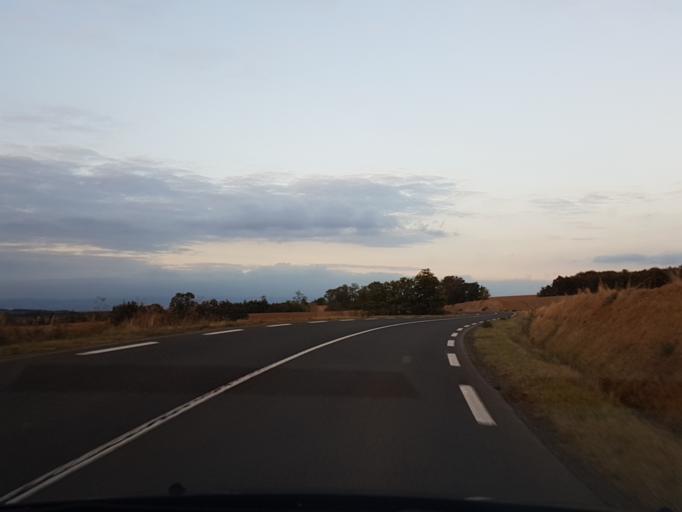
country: FR
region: Midi-Pyrenees
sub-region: Departement de l'Ariege
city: Mirepoix
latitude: 43.1486
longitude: 1.9616
